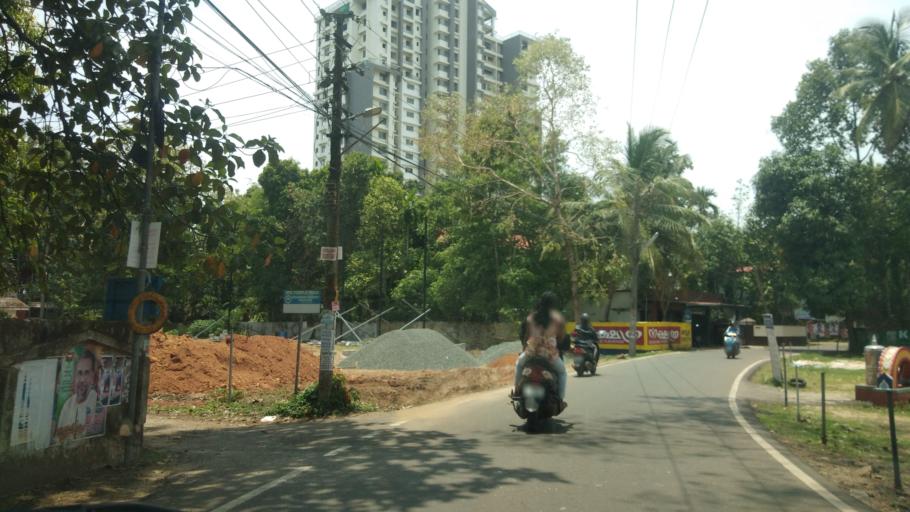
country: IN
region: Kerala
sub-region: Alappuzha
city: Arukutti
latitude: 9.8953
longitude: 76.3095
